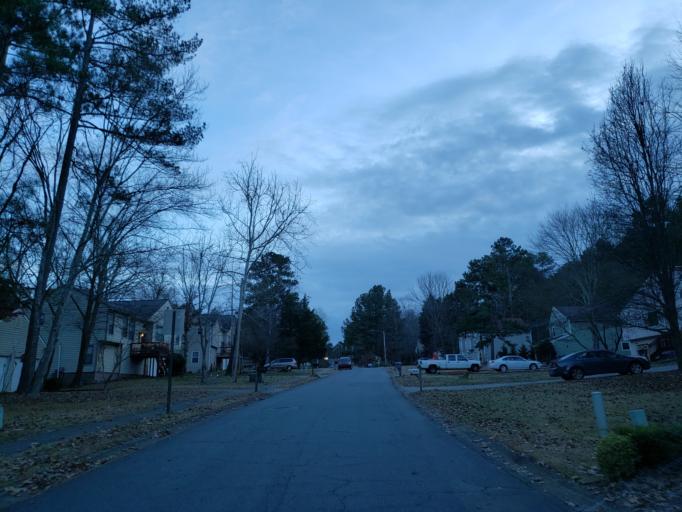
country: US
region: Georgia
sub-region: Cobb County
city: Kennesaw
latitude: 34.0477
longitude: -84.6450
